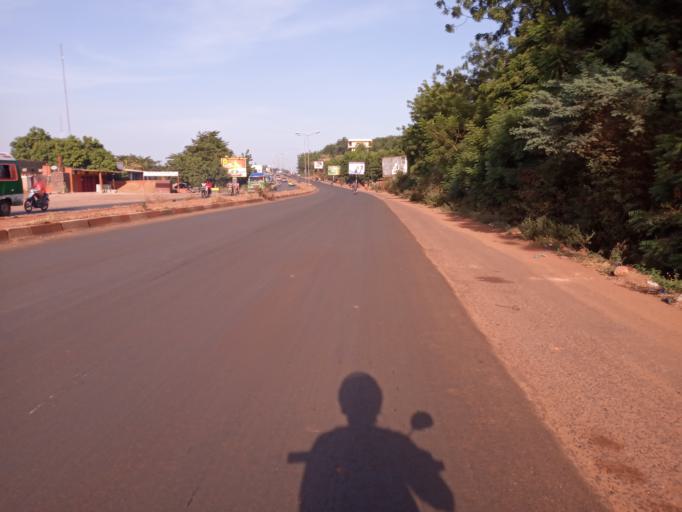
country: ML
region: Bamako
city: Bamako
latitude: 12.6157
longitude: -7.9893
